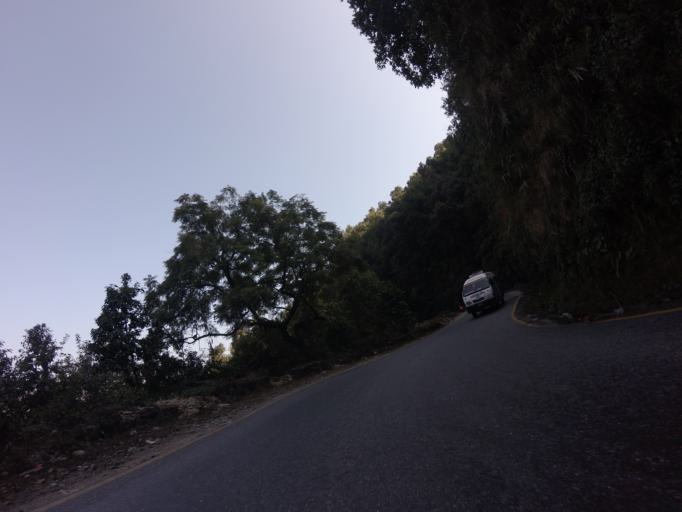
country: NP
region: Western Region
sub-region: Gandaki Zone
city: Pokhara
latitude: 28.1912
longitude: 83.8993
